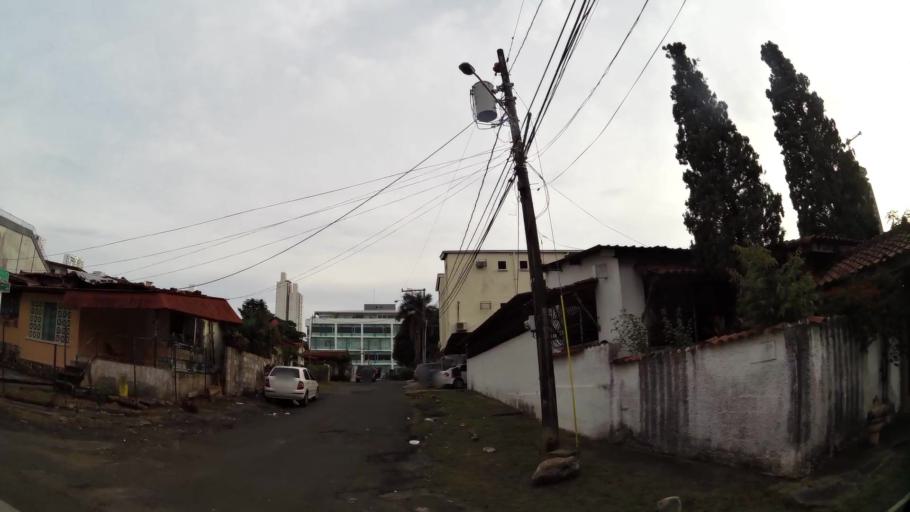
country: PA
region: Panama
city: Panama
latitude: 8.9953
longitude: -79.5030
